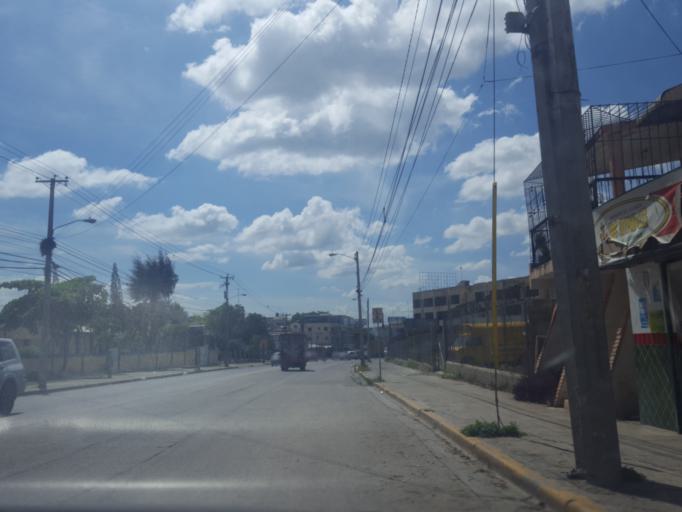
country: DO
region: Santiago
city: Santiago de los Caballeros
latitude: 19.4274
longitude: -70.6865
